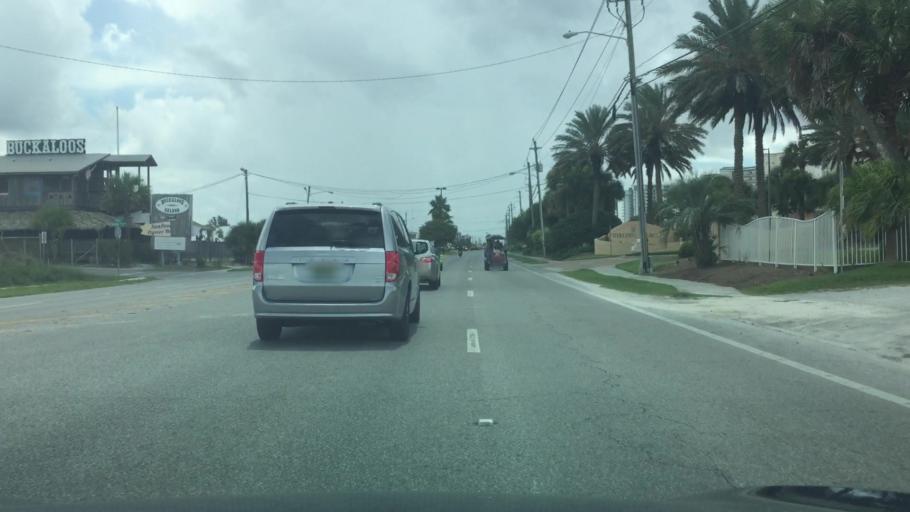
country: US
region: Florida
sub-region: Bay County
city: Lower Grand Lagoon
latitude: 30.1545
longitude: -85.7695
